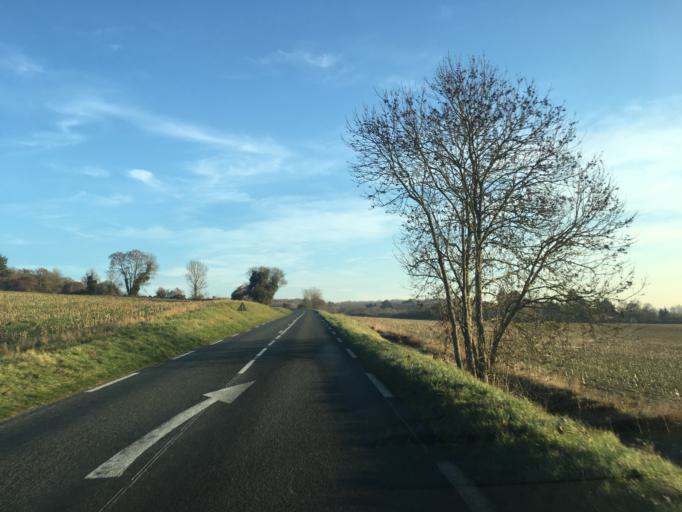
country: FR
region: Haute-Normandie
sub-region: Departement de l'Eure
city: Houlbec-Cocherel
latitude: 49.0563
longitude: 1.3382
